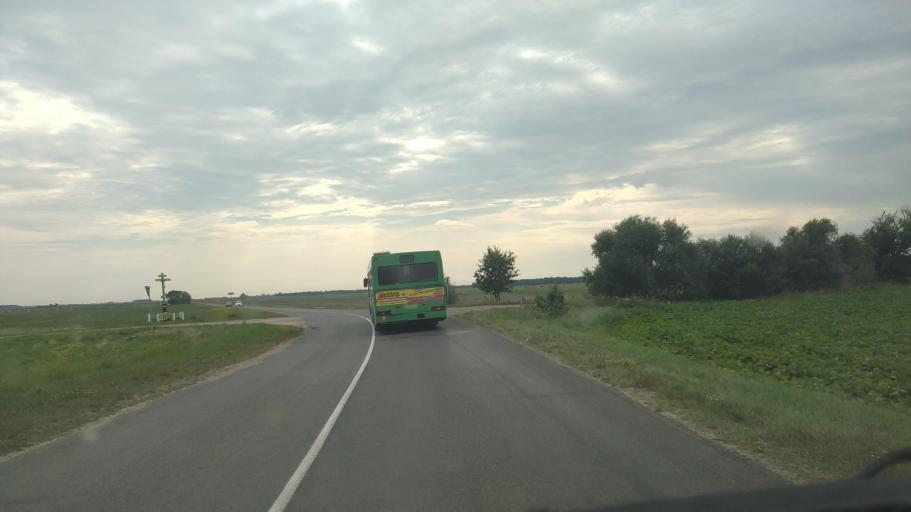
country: BY
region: Brest
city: Byaroza
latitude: 52.5769
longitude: 24.8606
